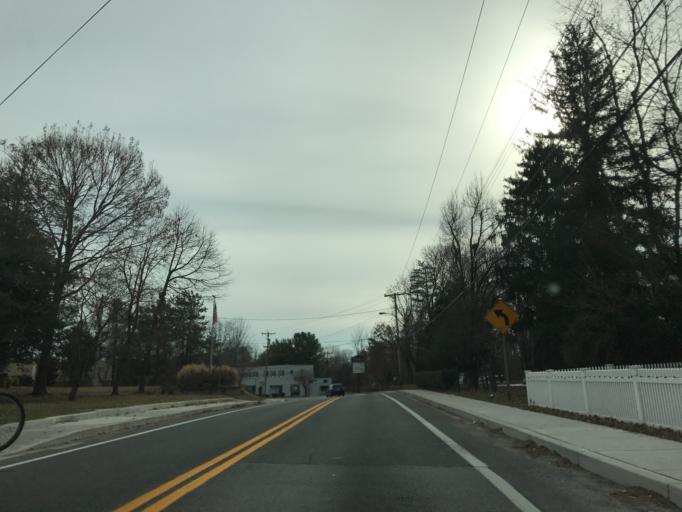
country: US
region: Maryland
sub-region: Anne Arundel County
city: Severna Park
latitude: 39.0751
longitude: -76.5485
